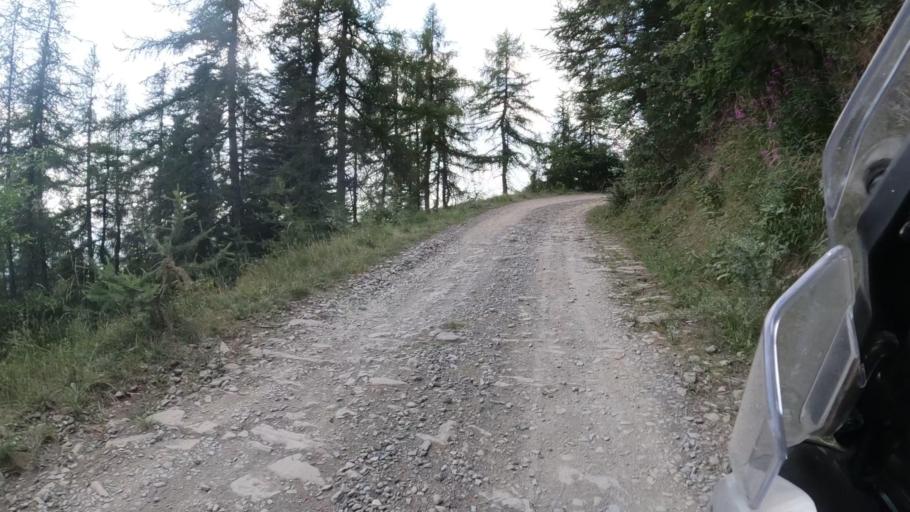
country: FR
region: Provence-Alpes-Cote d'Azur
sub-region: Departement des Alpes-Maritimes
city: Tende
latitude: 44.0290
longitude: 7.6667
